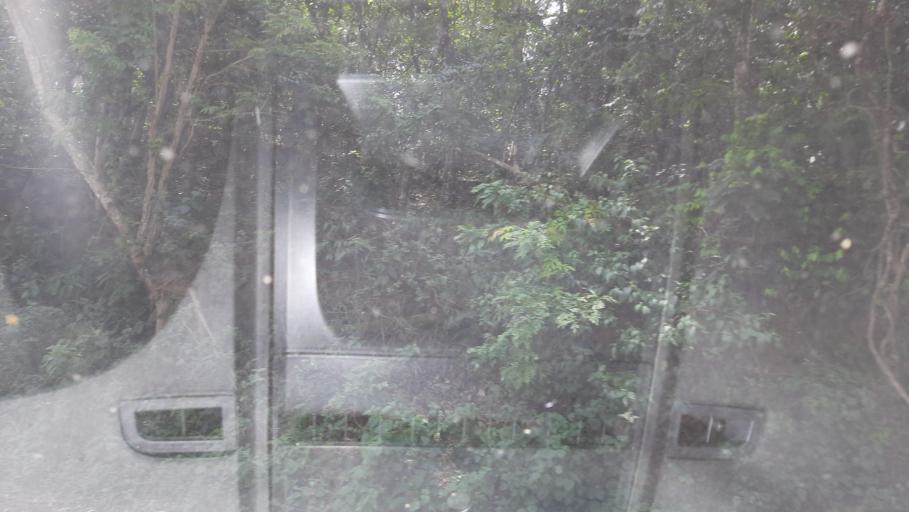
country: BR
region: Sao Paulo
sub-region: Caieiras
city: Caieiras
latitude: -23.4167
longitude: -46.7225
